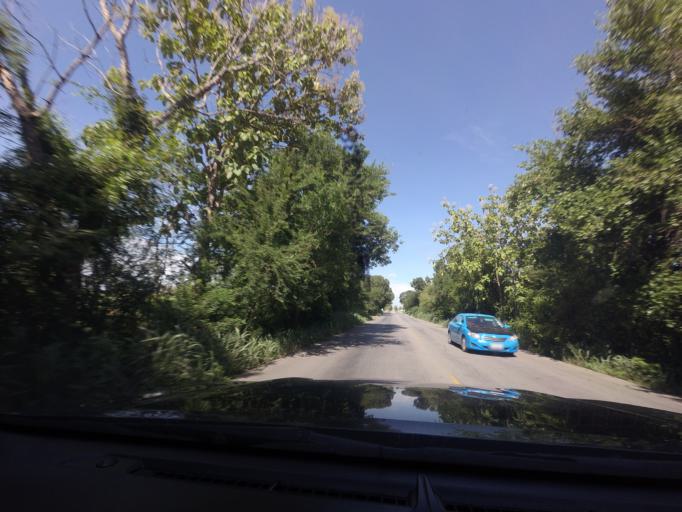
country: TH
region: Suphan Buri
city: Song Phi Nong
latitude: 14.1665
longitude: 99.9177
